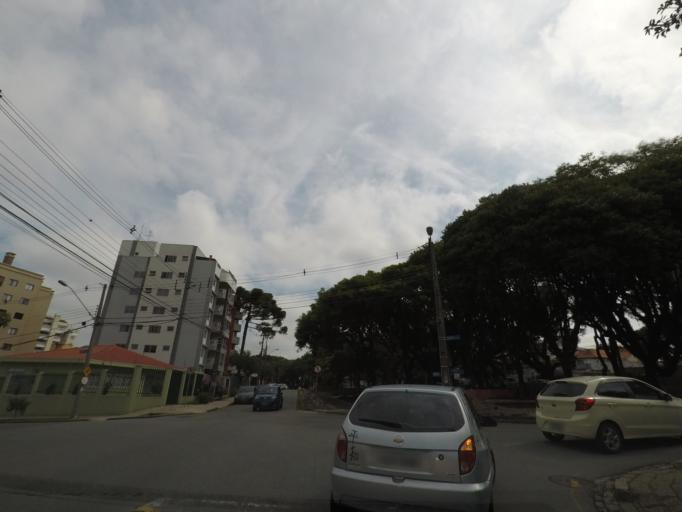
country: BR
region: Parana
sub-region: Curitiba
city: Curitiba
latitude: -25.4542
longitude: -49.2950
